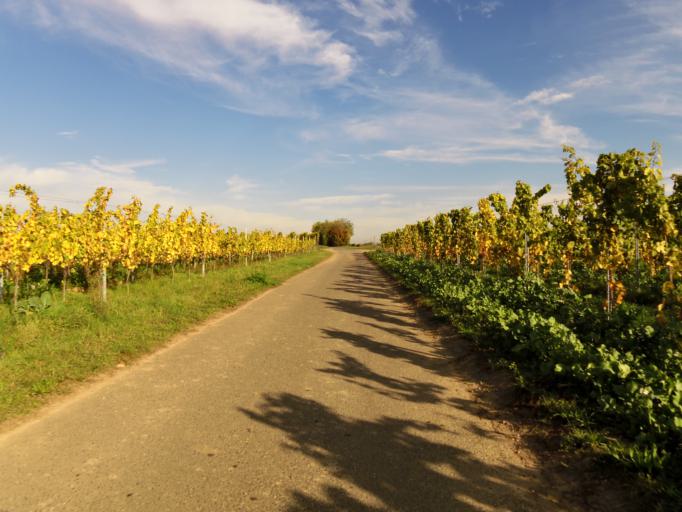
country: DE
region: Rheinland-Pfalz
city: Friedelsheim
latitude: 49.4427
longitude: 8.2048
